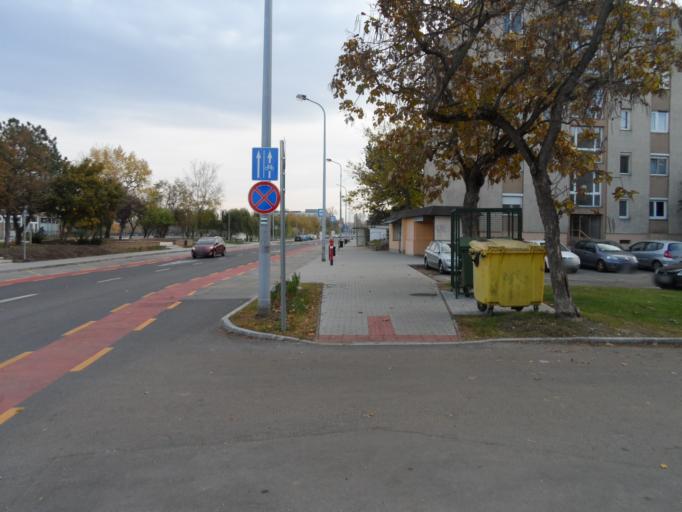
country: HU
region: Fejer
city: Szekesfehervar
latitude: 47.2010
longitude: 18.3970
